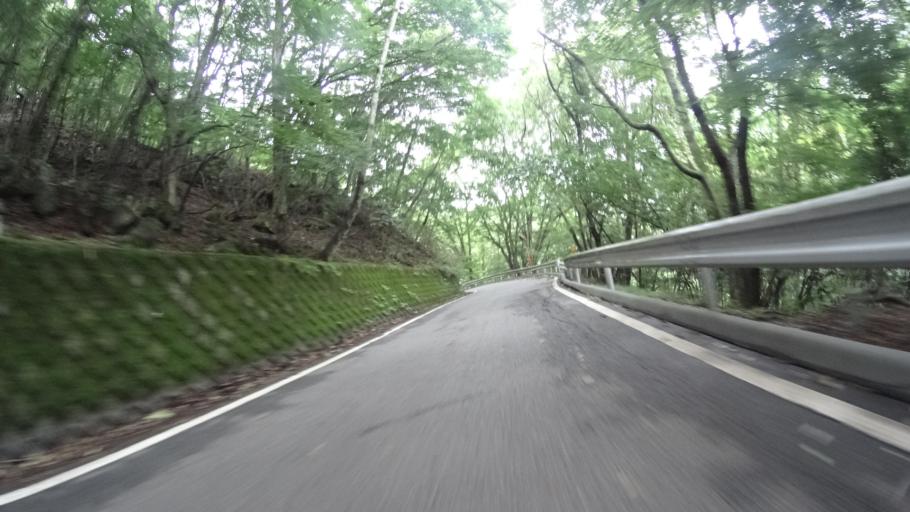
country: JP
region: Yamanashi
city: Enzan
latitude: 35.7975
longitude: 138.6840
